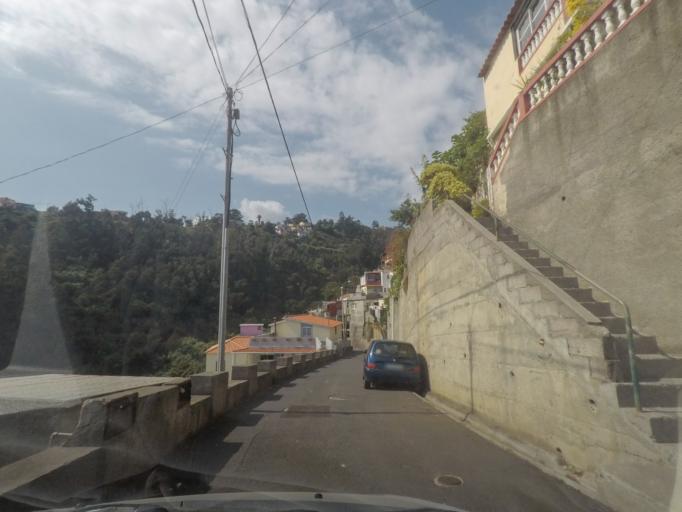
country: PT
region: Madeira
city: Camara de Lobos
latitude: 32.6725
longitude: -16.9511
